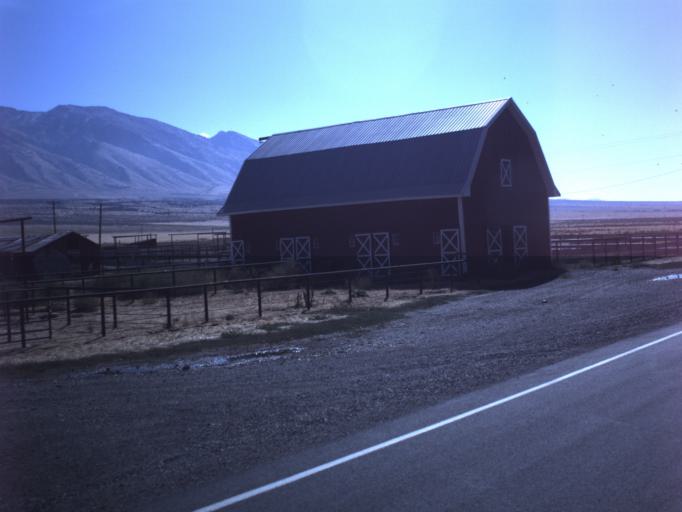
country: US
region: Utah
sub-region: Tooele County
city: Grantsville
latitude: 40.4934
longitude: -112.7480
